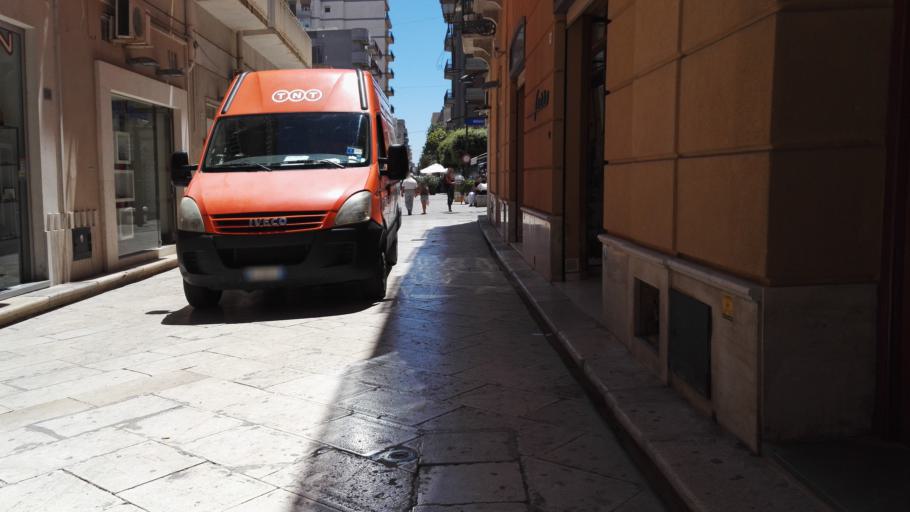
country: IT
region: Sicily
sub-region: Trapani
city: Marsala
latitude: 37.7984
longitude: 12.4367
